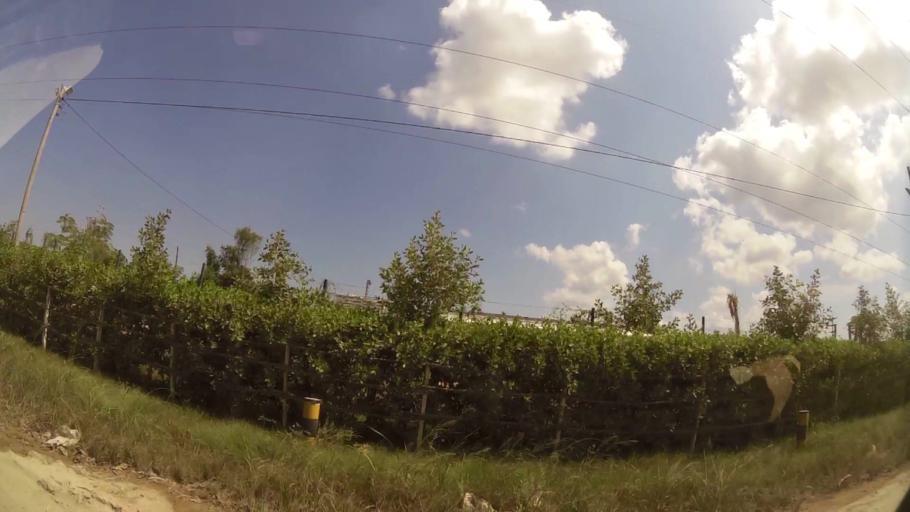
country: CO
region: Bolivar
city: Cartagena
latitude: 10.3456
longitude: -75.4867
